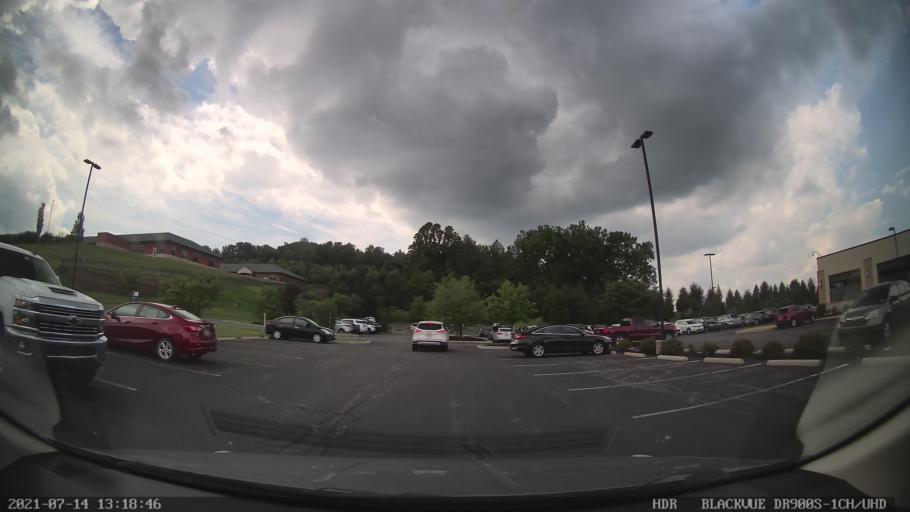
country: US
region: Pennsylvania
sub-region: Berks County
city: Spring Ridge
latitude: 40.3604
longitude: -75.9897
